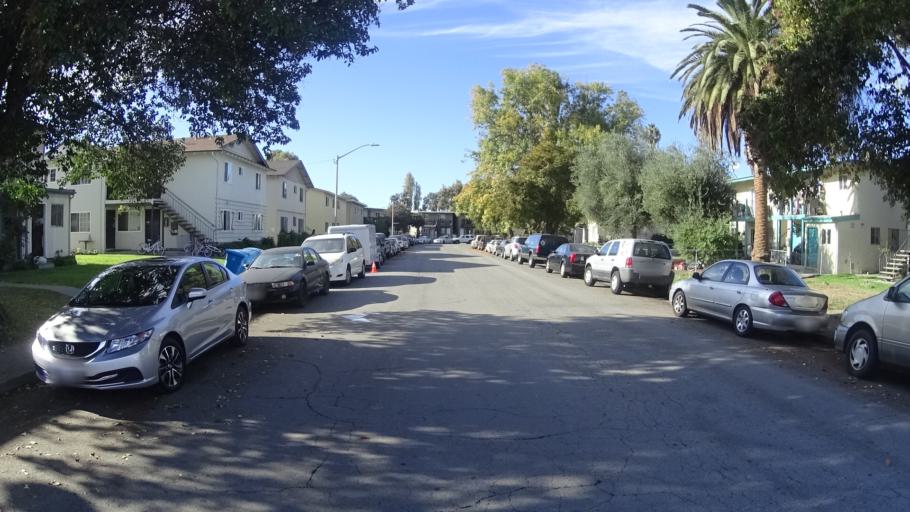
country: US
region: California
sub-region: Santa Clara County
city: Santa Clara
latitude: 37.3633
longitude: -121.9642
